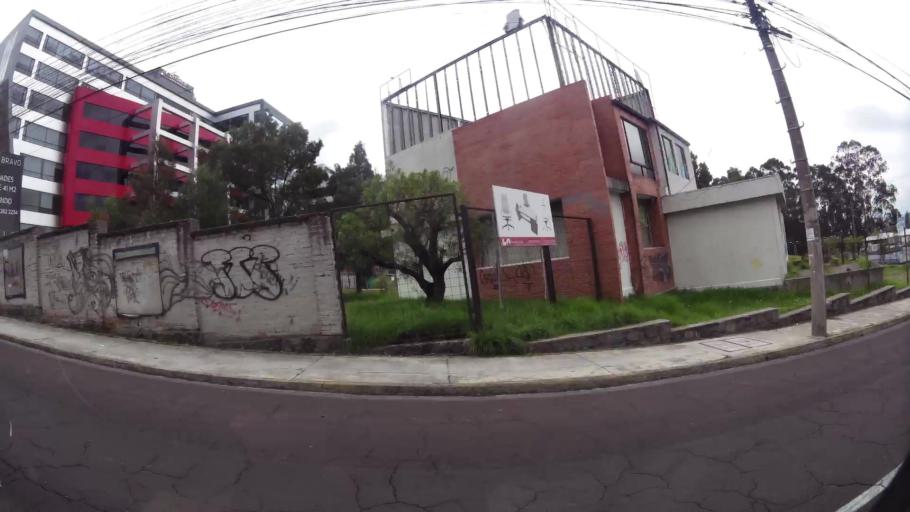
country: EC
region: Pichincha
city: Quito
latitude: -0.1838
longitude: -78.5023
